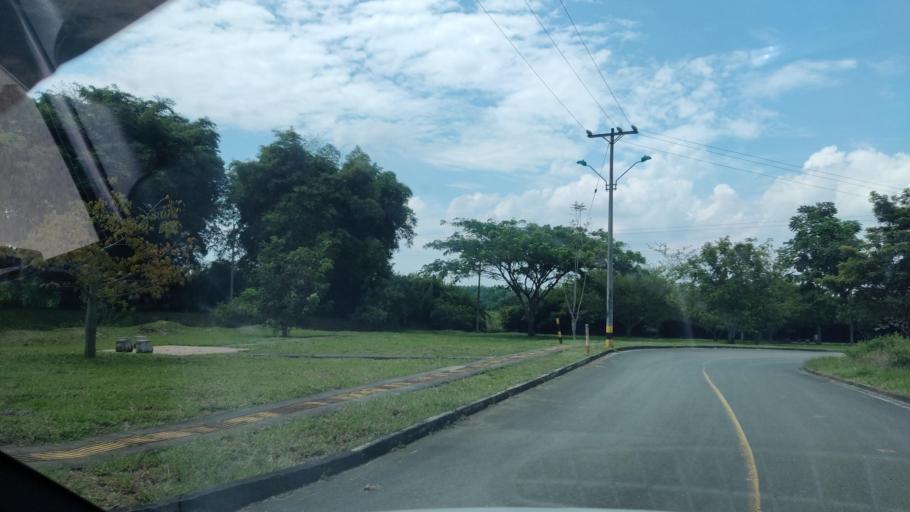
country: CO
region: Valle del Cauca
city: Jamundi
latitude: 3.3018
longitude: -76.5551
